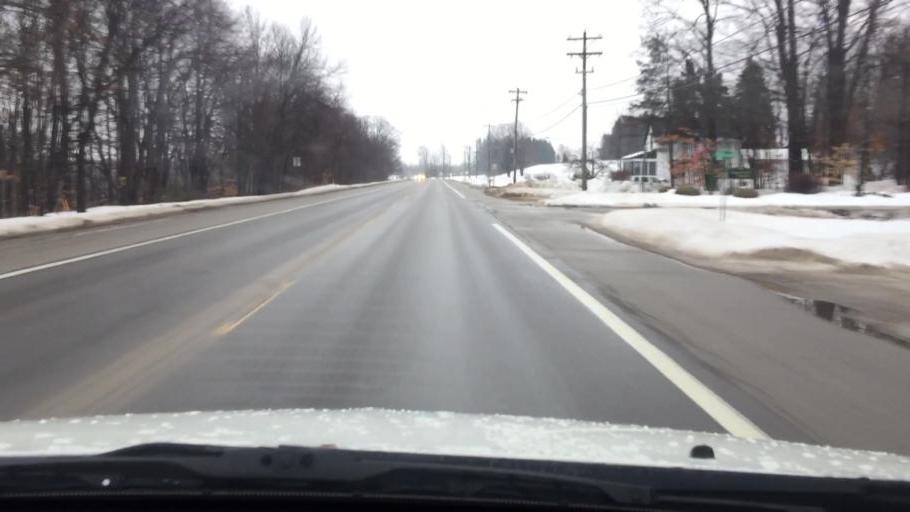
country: US
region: Michigan
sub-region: Charlevoix County
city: Charlevoix
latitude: 45.2867
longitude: -85.2435
